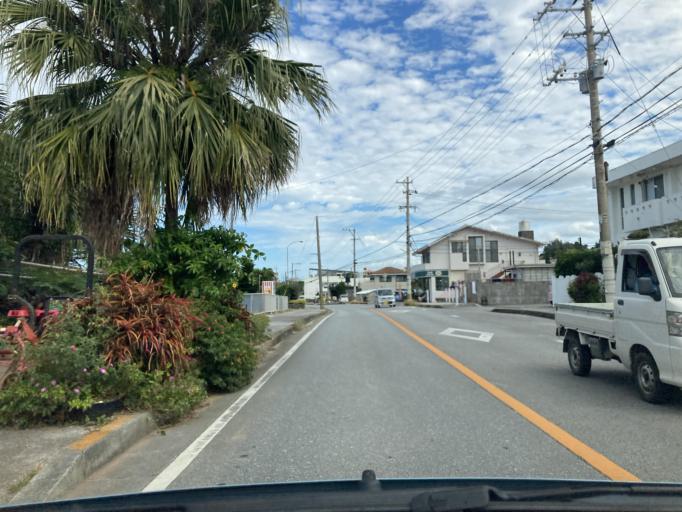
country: JP
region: Okinawa
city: Ishikawa
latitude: 26.4268
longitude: 127.7507
